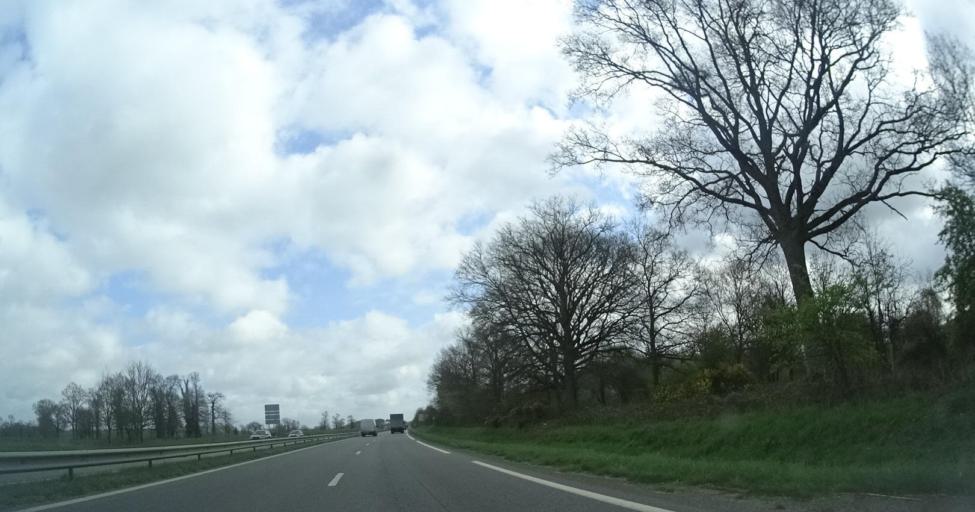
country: FR
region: Brittany
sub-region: Departement d'Ille-et-Vilaine
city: Bruz
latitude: 48.0483
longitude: -1.7510
